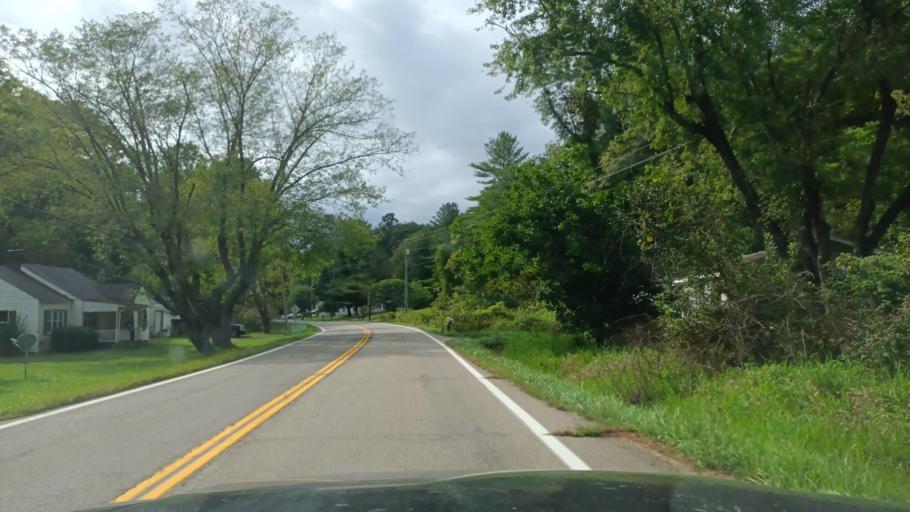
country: US
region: Ohio
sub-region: Vinton County
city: McArthur
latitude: 39.2715
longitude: -82.5697
